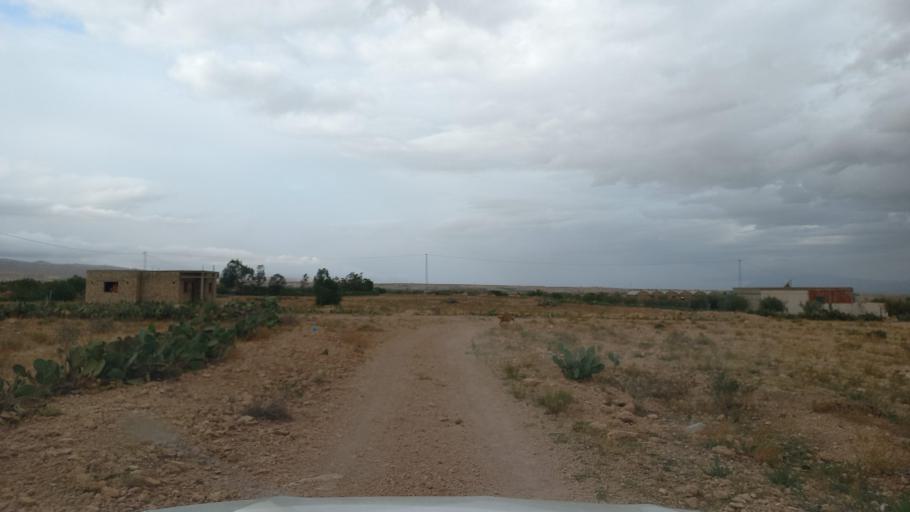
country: TN
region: Al Qasrayn
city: Kasserine
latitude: 35.2791
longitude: 8.9521
